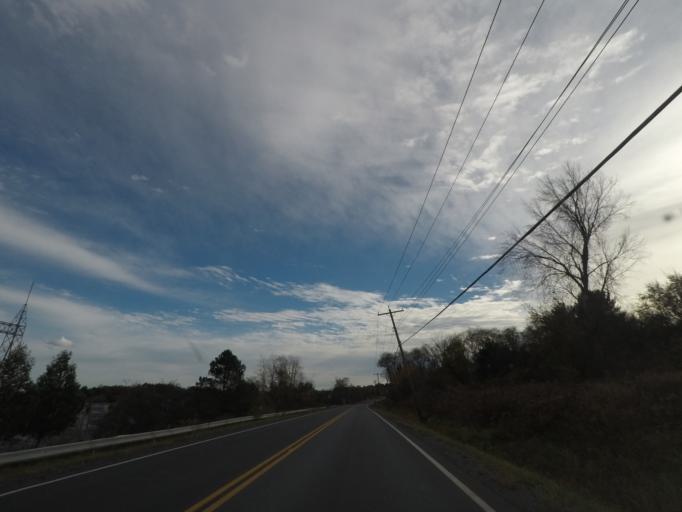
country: US
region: New York
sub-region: Albany County
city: Voorheesville
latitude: 42.6086
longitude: -73.9055
